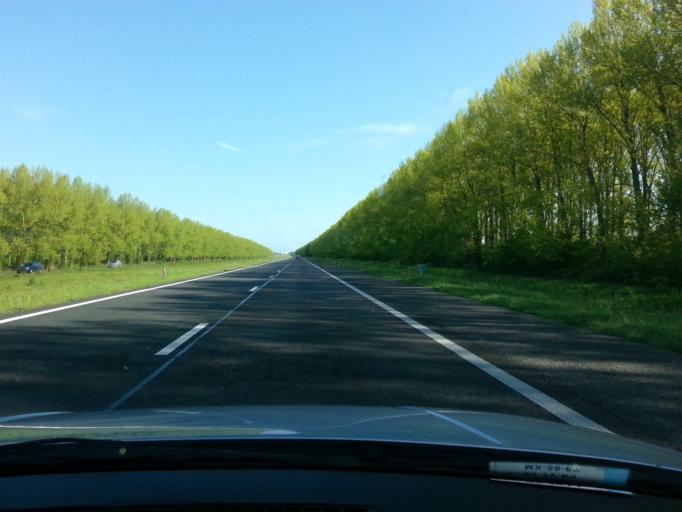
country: NL
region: Flevoland
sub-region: Gemeente Lelystad
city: Lelystad
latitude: 52.5194
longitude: 5.5336
